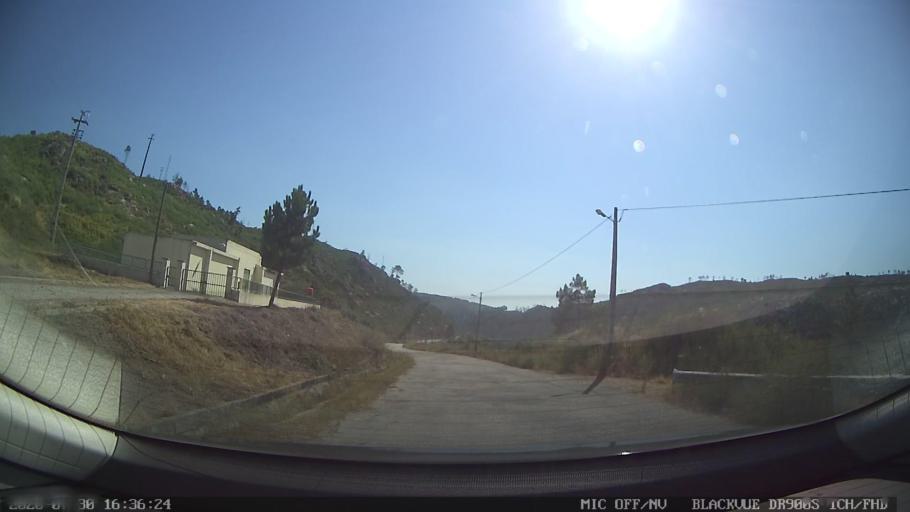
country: PT
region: Vila Real
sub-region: Sabrosa
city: Sabrosa
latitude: 41.3099
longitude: -7.4875
